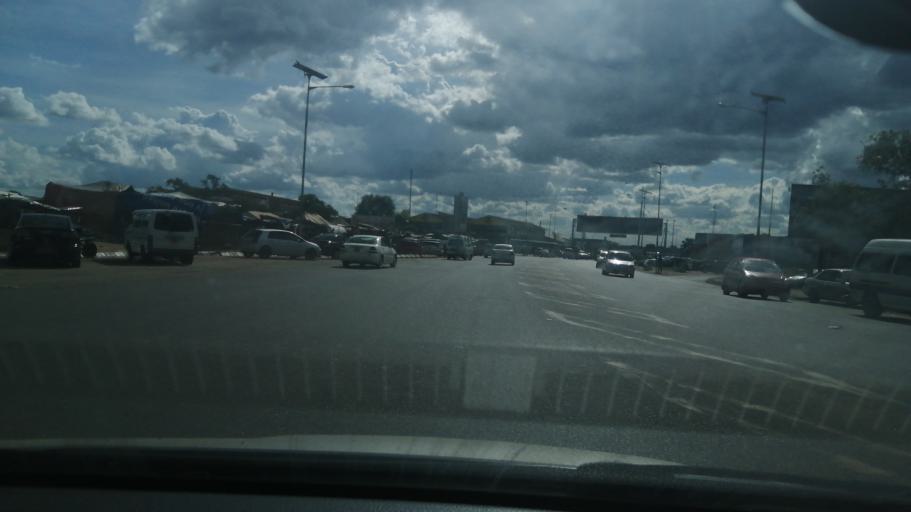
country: ZW
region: Harare
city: Harare
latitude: -17.8522
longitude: 31.0551
